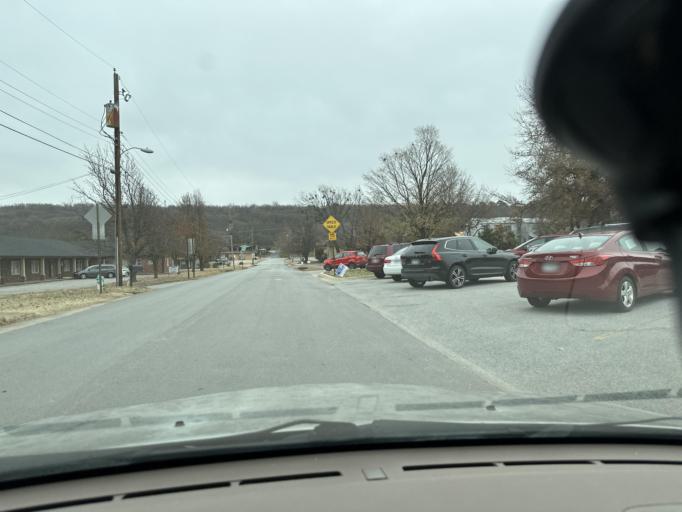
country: US
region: Arkansas
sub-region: Washington County
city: Fayetteville
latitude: 36.0886
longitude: -94.1572
